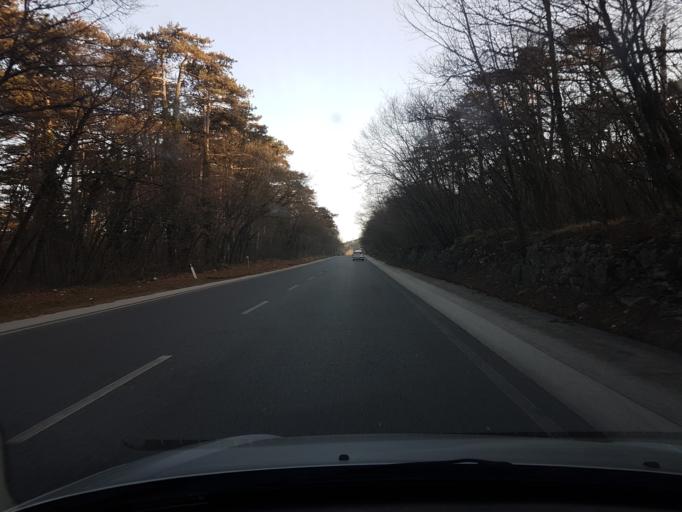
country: IT
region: Friuli Venezia Giulia
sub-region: Provincia di Trieste
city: Villa Opicina
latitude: 45.6947
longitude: 13.7658
